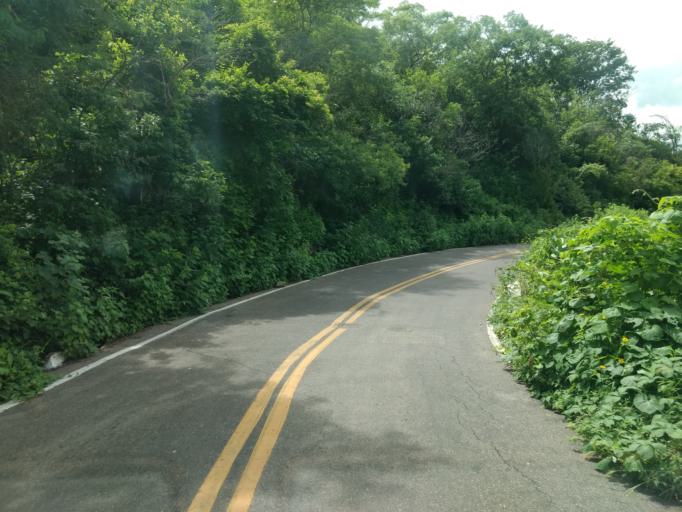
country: BR
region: Ceara
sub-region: Crateus
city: Crateus
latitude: -5.2429
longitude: -40.8994
